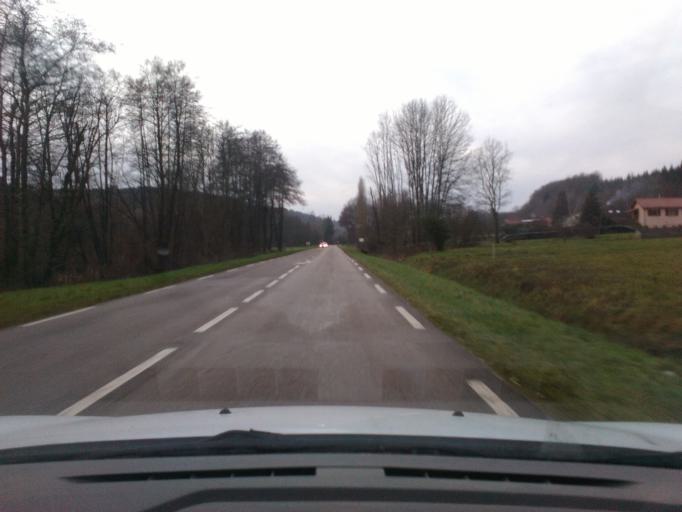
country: FR
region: Lorraine
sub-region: Departement des Vosges
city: Senones
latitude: 48.3875
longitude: 6.9510
